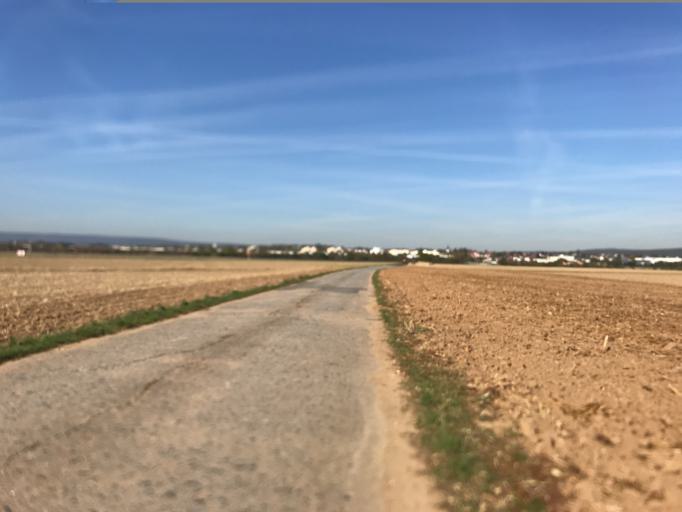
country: DE
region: Hesse
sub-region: Regierungsbezirk Darmstadt
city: Hochheim am Main
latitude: 50.0475
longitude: 8.3391
